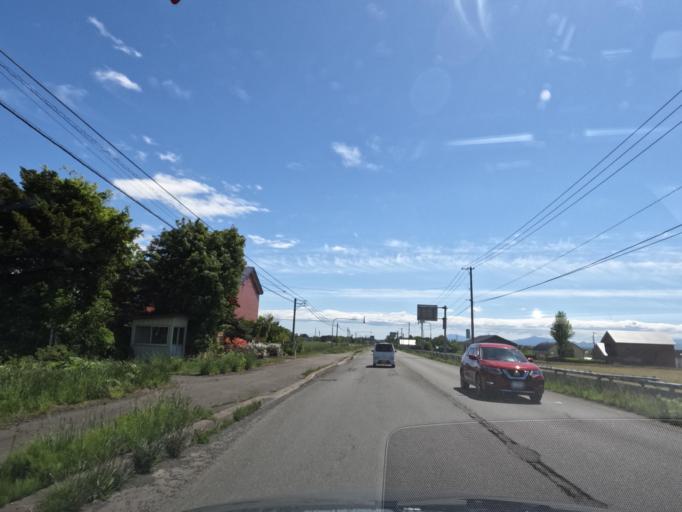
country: JP
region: Hokkaido
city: Kitahiroshima
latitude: 43.0307
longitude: 141.7144
